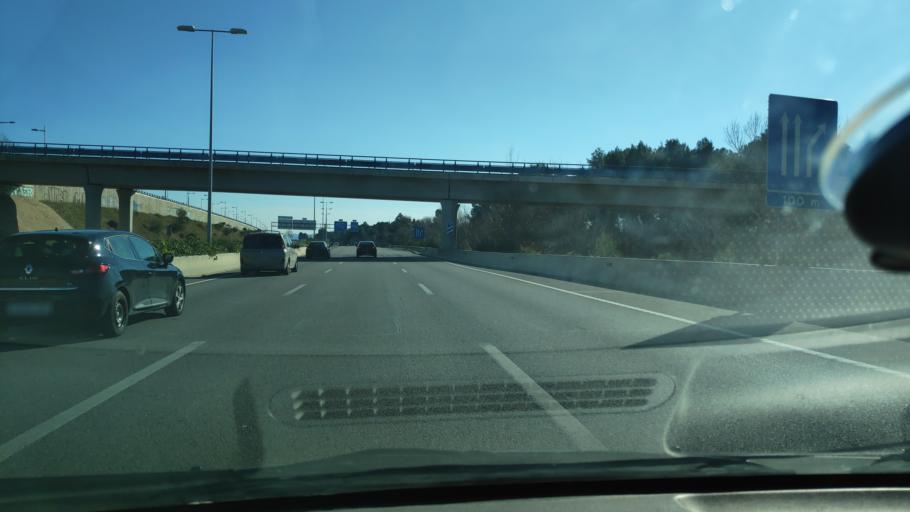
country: ES
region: Catalonia
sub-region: Provincia de Barcelona
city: Sant Quirze del Valles
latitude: 41.5454
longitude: 2.0776
